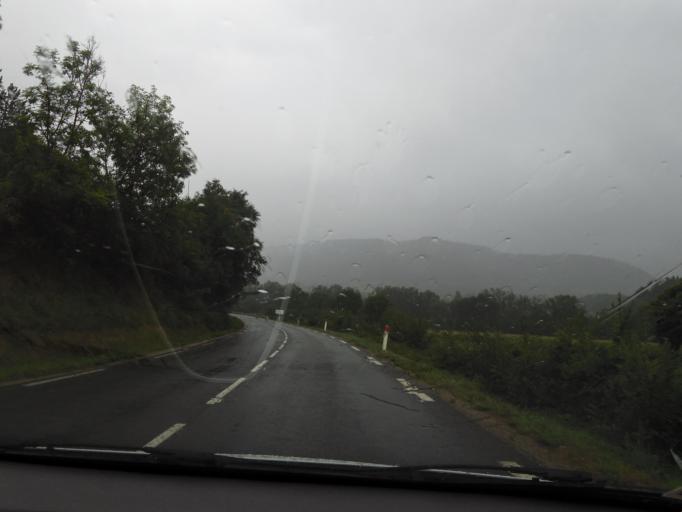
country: FR
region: Languedoc-Roussillon
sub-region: Departement de la Lozere
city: Chanac
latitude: 44.4704
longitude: 3.3391
